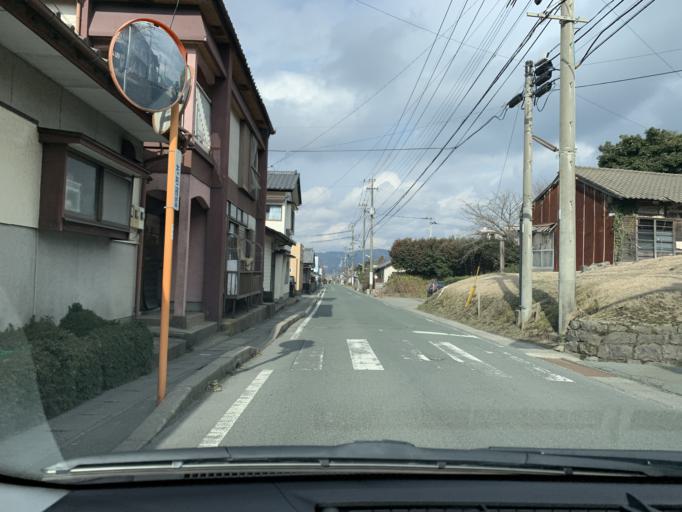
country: JP
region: Kumamoto
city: Aso
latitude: 32.9398
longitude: 131.1152
